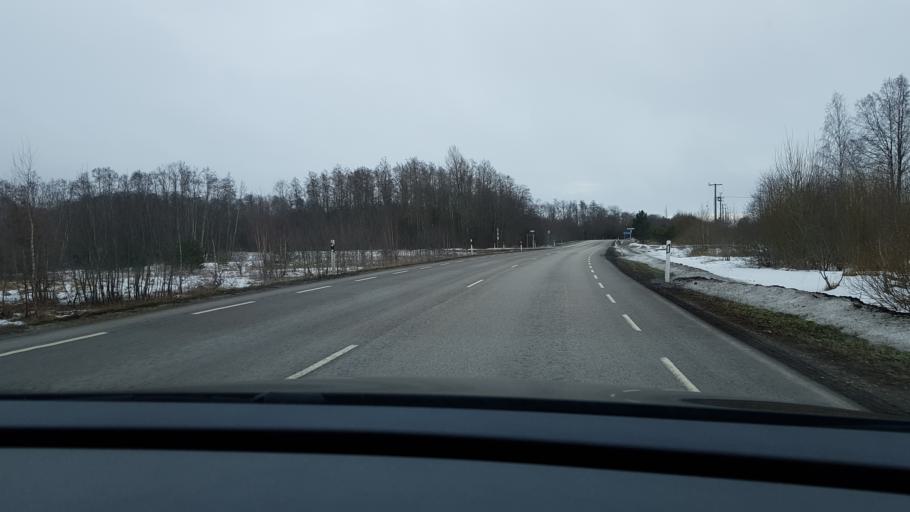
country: EE
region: Paernumaa
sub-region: Sauga vald
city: Sauga
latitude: 58.4199
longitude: 24.4424
